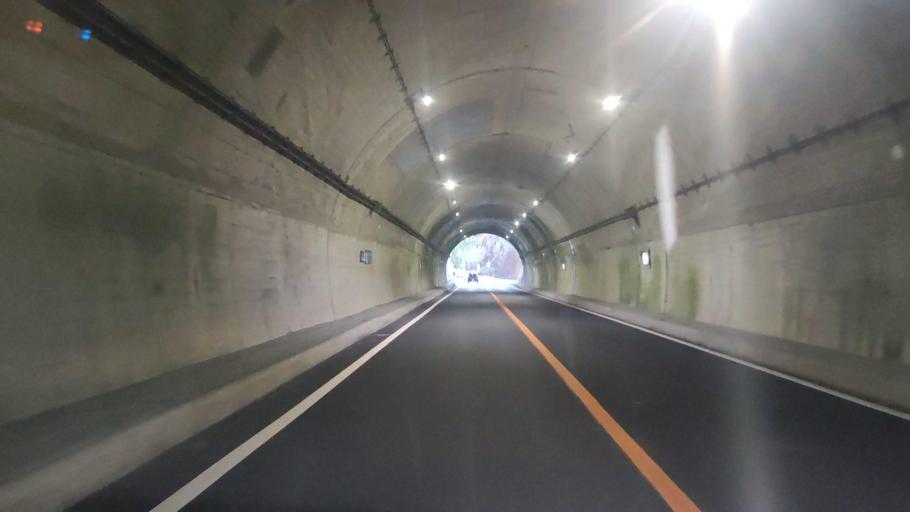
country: JP
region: Miyazaki
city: Nobeoka
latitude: 32.6307
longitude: 131.7229
